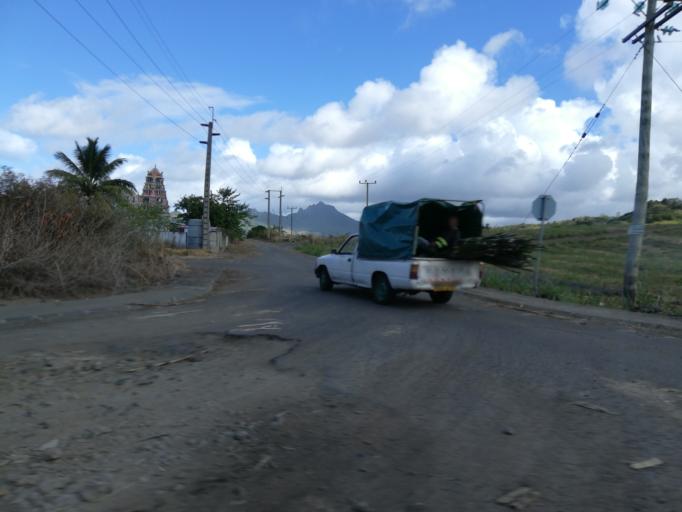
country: MU
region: Flacq
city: Bel Air Riviere Seche
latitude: -20.2638
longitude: 57.7399
